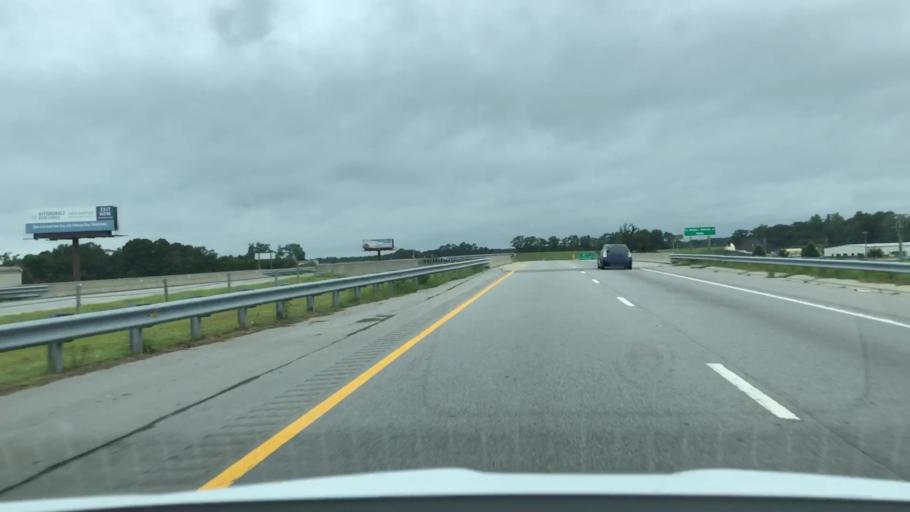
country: US
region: North Carolina
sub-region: Lenoir County
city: Kinston
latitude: 35.2622
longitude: -77.6668
